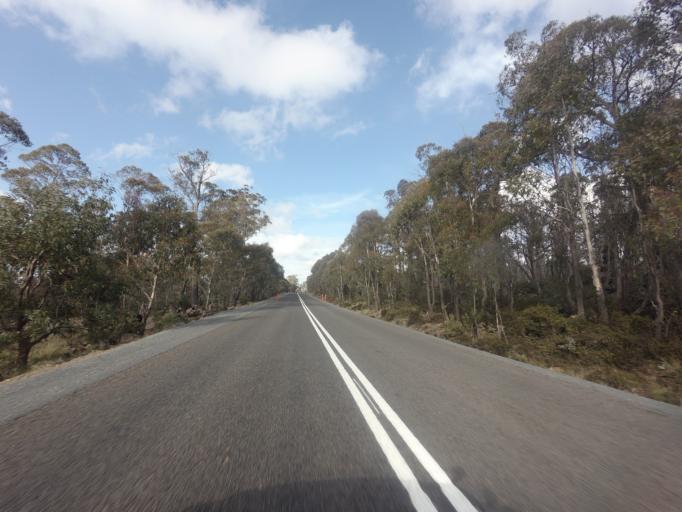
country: AU
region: Tasmania
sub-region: Meander Valley
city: Deloraine
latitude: -41.8419
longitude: 146.6855
